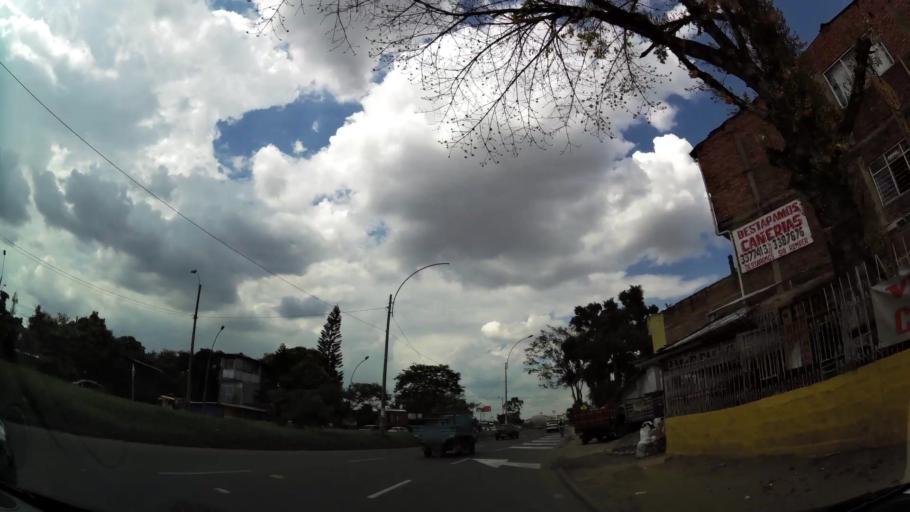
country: CO
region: Valle del Cauca
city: Cali
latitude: 3.4020
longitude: -76.5227
